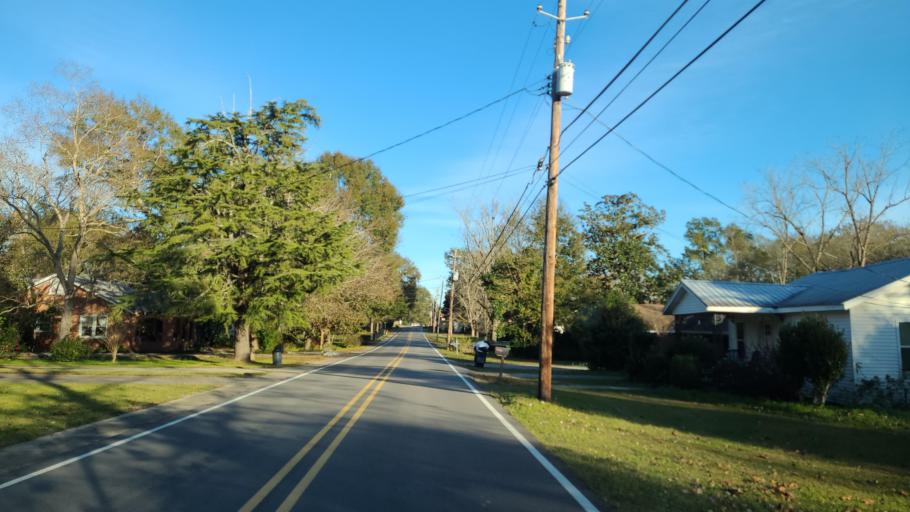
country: US
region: Mississippi
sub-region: Lamar County
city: Purvis
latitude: 31.1452
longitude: -89.4156
